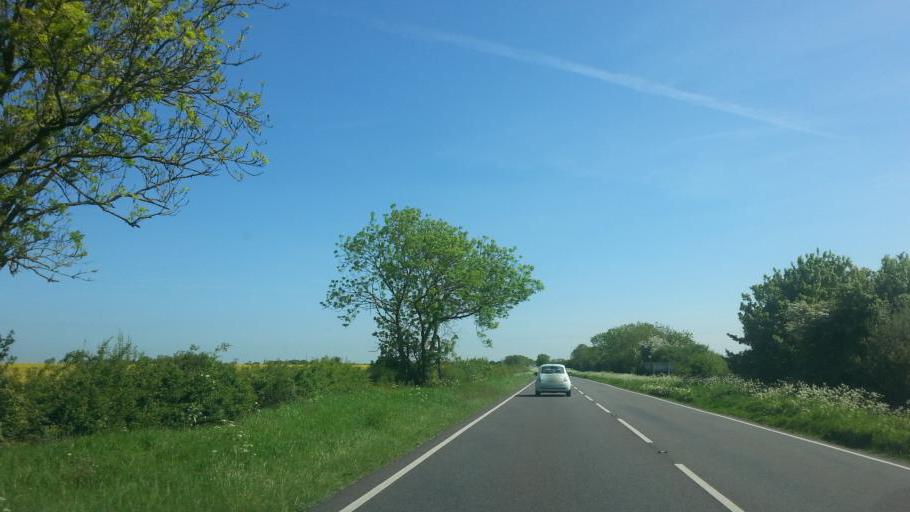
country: GB
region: England
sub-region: Cambridgeshire
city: Hemingford Grey
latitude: 52.3654
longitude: -0.1130
